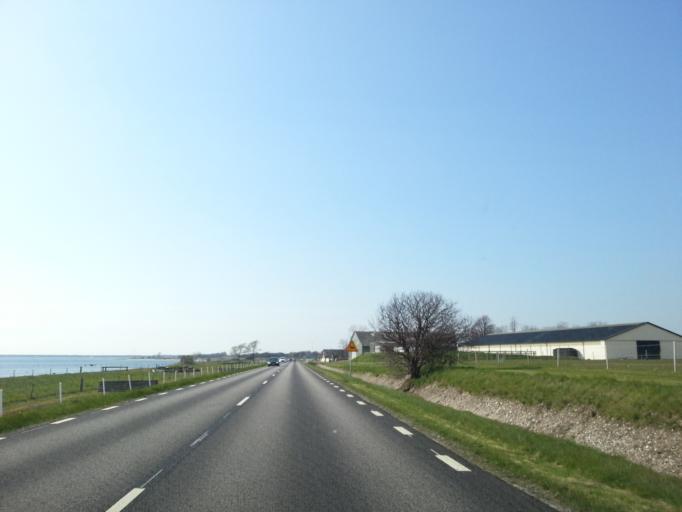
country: SE
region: Skane
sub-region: Trelleborgs Kommun
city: Skare
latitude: 55.3868
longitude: 13.0174
